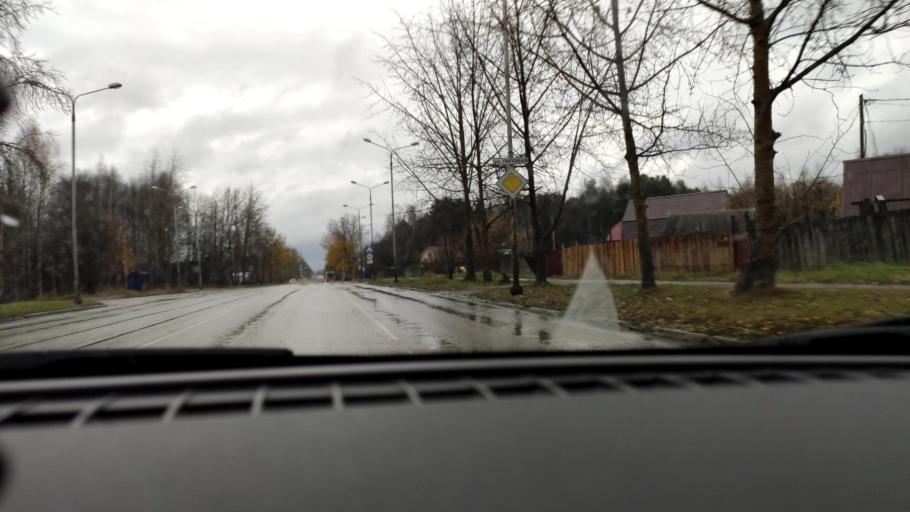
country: RU
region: Perm
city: Perm
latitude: 58.0793
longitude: 56.3727
